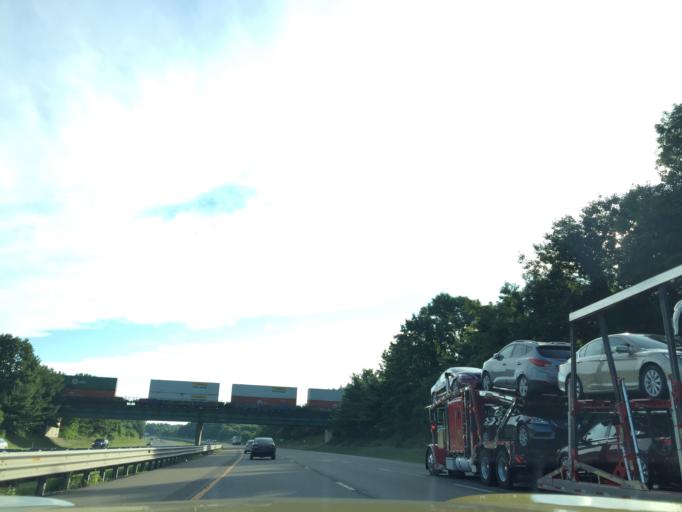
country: US
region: New Jersey
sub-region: Warren County
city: Alpha
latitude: 40.6544
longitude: -75.1488
